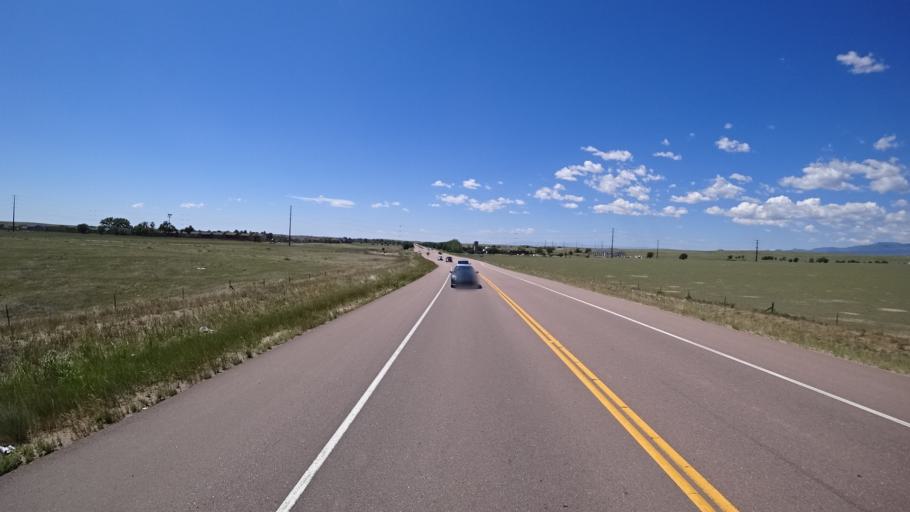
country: US
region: Colorado
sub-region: El Paso County
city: Security-Widefield
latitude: 38.7845
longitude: -104.6594
